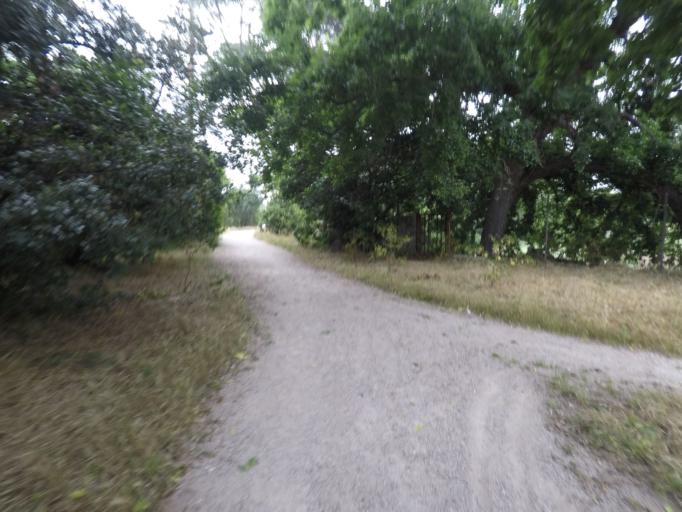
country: FR
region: Provence-Alpes-Cote d'Azur
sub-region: Departement des Bouches-du-Rhone
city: Marseille 09
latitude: 43.2573
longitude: 5.4130
